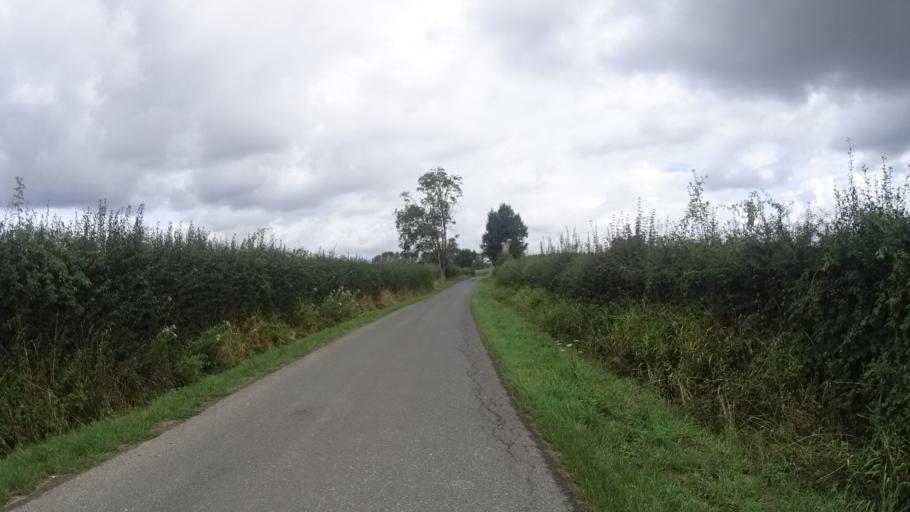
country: FR
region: Nord-Pas-de-Calais
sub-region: Departement du Nord
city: Landrecies
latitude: 50.1315
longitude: 3.7260
